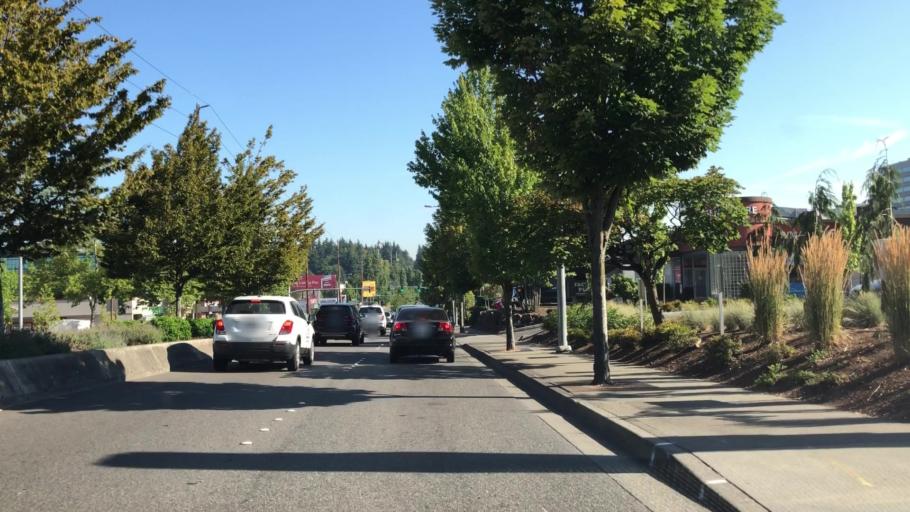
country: US
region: Washington
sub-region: King County
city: Newport
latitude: 47.5749
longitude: -122.1693
